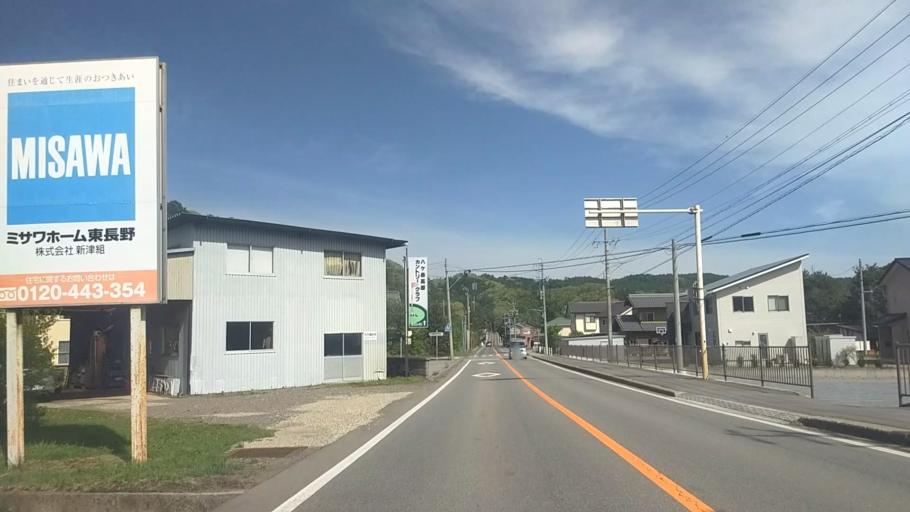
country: JP
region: Nagano
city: Saku
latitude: 36.0356
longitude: 138.4767
